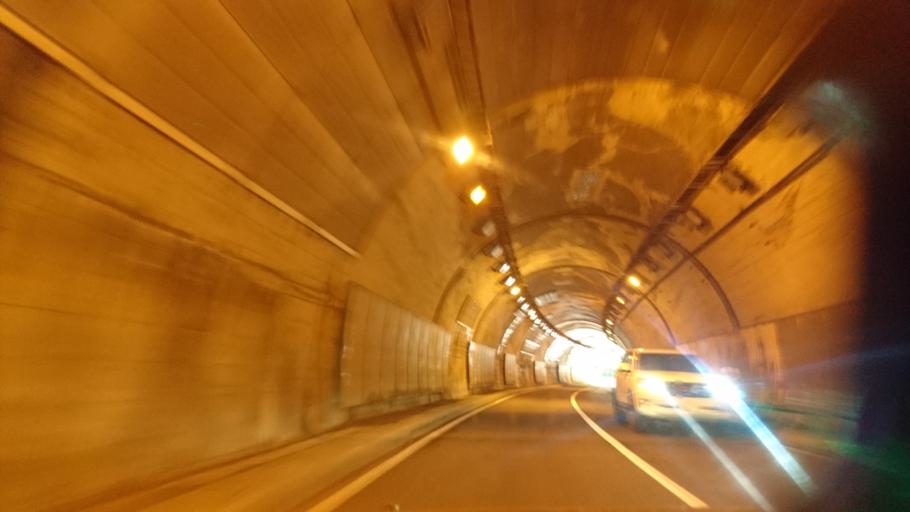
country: JP
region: Iwate
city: Shizukuishi
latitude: 39.6931
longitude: 140.7839
